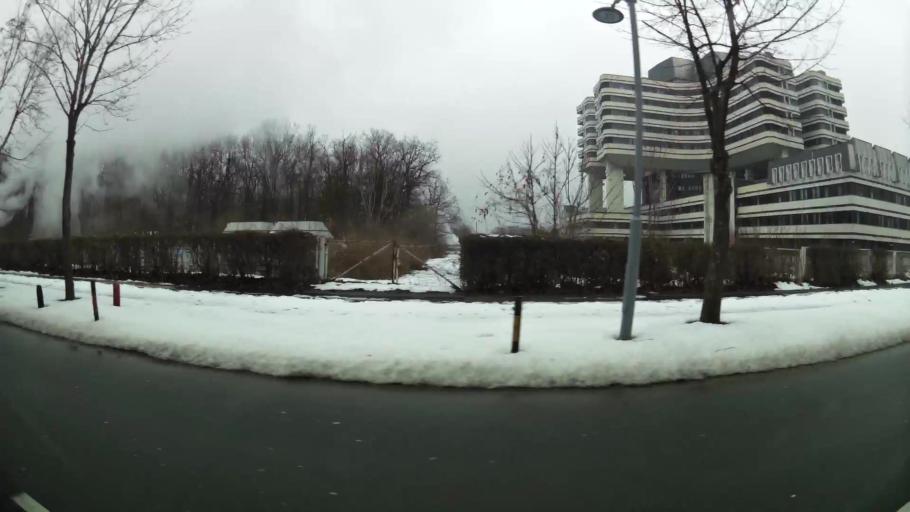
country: RS
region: Central Serbia
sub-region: Belgrade
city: Vozdovac
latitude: 44.7642
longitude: 20.4649
